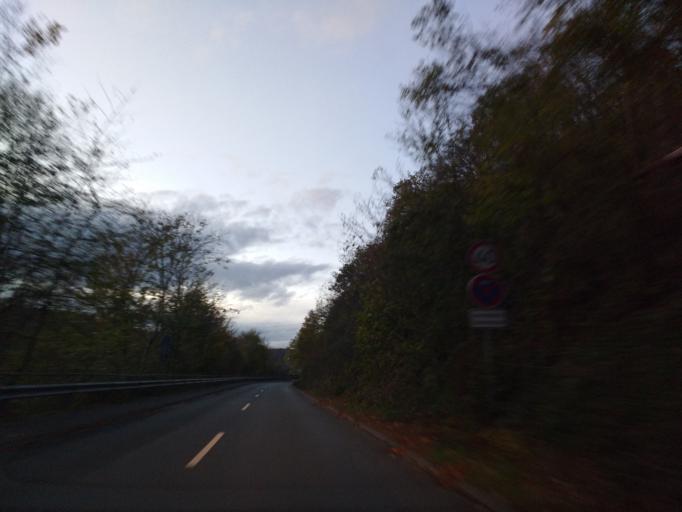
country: DE
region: Hesse
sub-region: Regierungsbezirk Kassel
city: Waldeck
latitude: 51.1838
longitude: 9.0622
